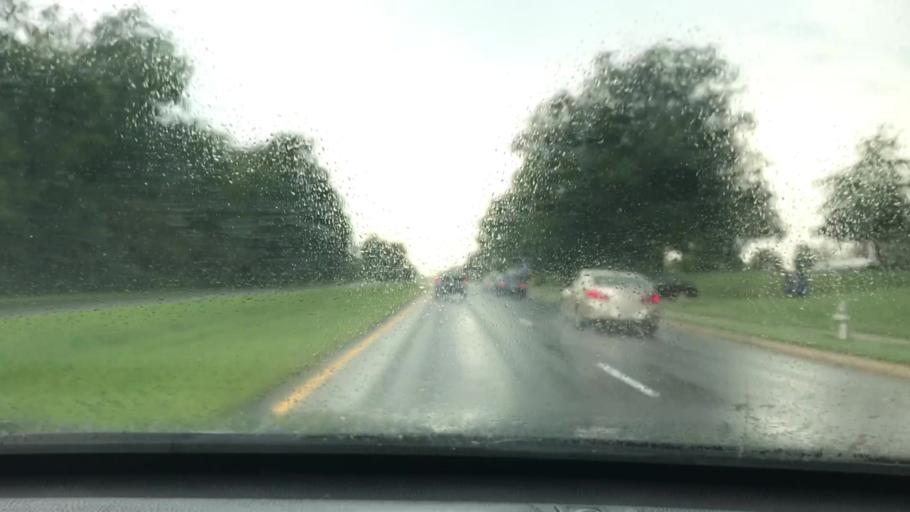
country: US
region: Virginia
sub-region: Henrico County
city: Laurel
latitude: 37.6299
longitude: -77.5246
